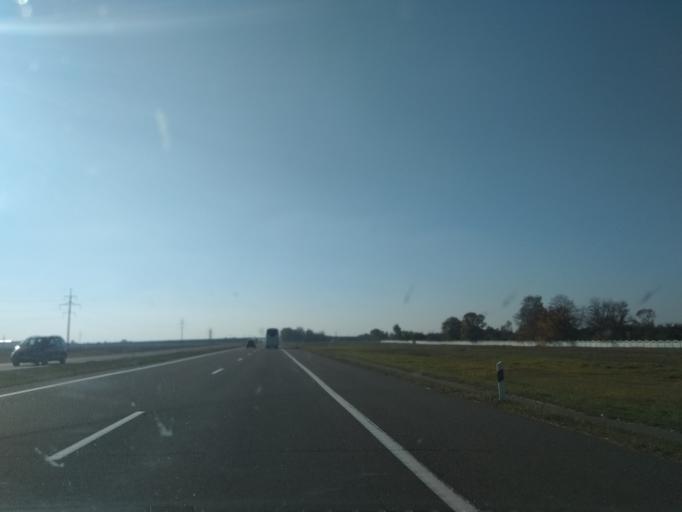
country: BY
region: Brest
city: Zhabinka
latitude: 52.1287
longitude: 23.9126
